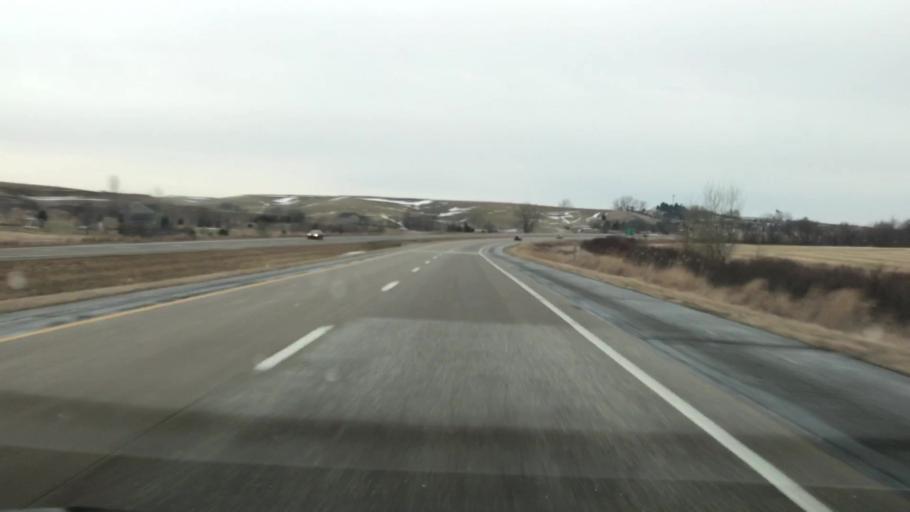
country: US
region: Iowa
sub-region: Pottawattamie County
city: Oakland
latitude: 41.4470
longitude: -95.6041
